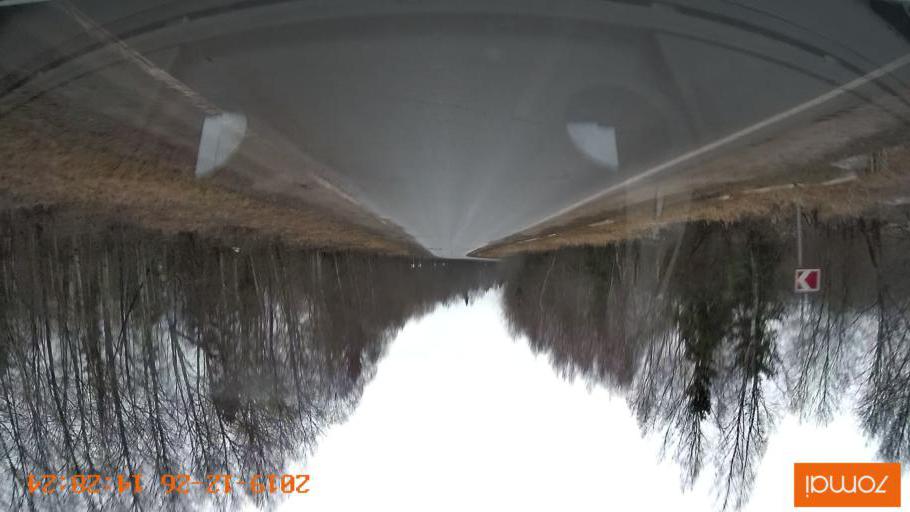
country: RU
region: Jaroslavl
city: Poshekhon'ye
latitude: 58.4757
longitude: 39.0539
